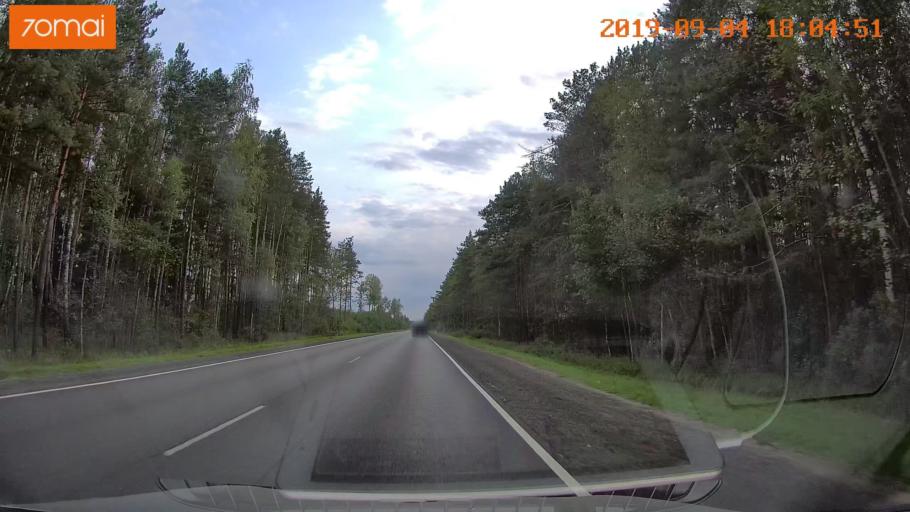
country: RU
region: Moskovskaya
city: Il'inskiy Pogost
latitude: 55.4475
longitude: 38.8337
